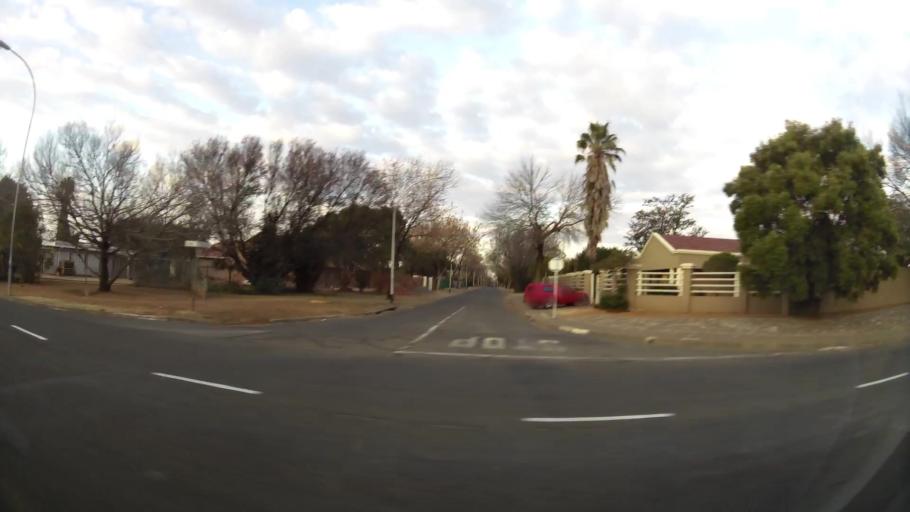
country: ZA
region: Orange Free State
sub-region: Mangaung Metropolitan Municipality
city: Bloemfontein
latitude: -29.1402
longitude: 26.1755
